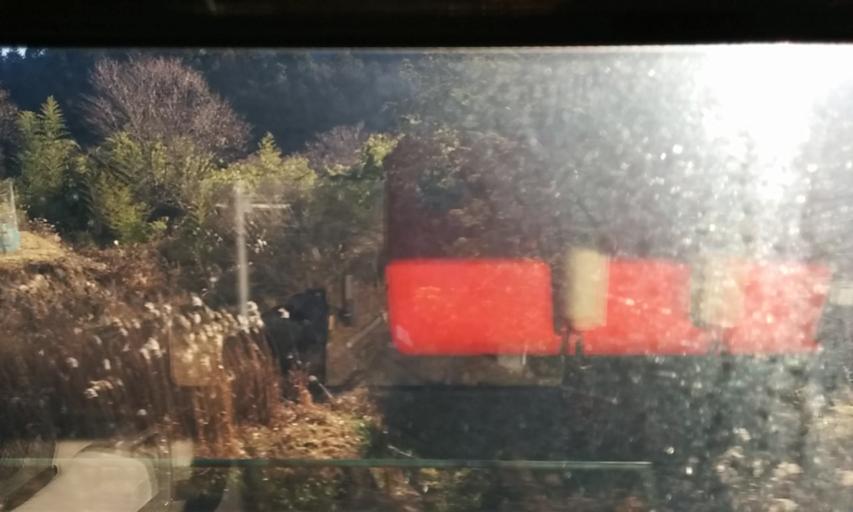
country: JP
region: Nagano
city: Ina
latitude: 35.7738
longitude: 137.6985
